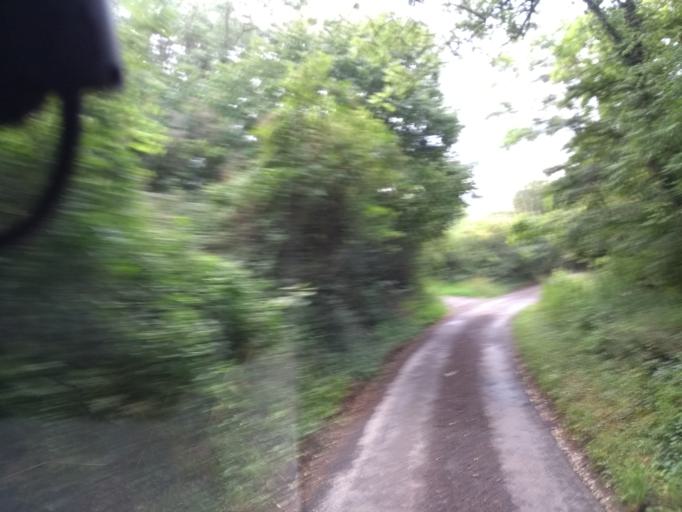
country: GB
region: England
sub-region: Somerset
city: Castle Cary
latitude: 51.0269
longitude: -2.5785
